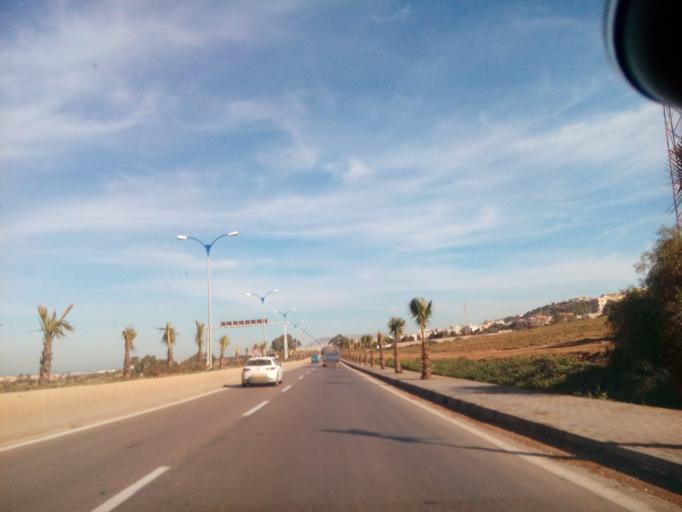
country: DZ
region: Mostaganem
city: Mostaganem
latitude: 35.8920
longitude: 0.0580
